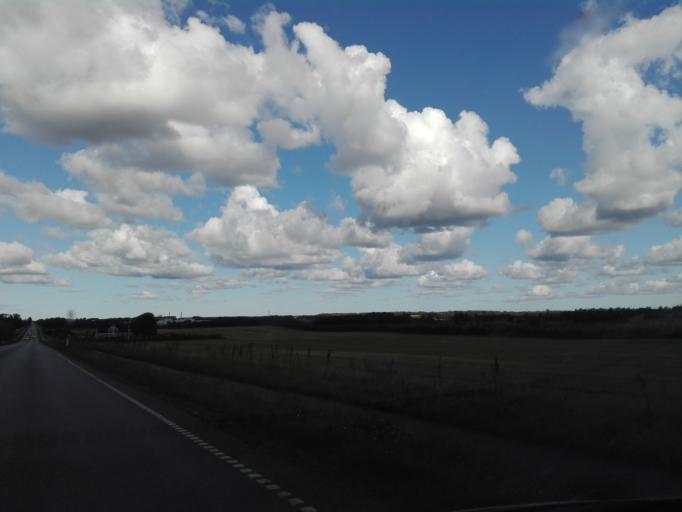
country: DK
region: North Denmark
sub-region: Mariagerfjord Kommune
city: Hobro
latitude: 56.6059
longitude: 9.8066
